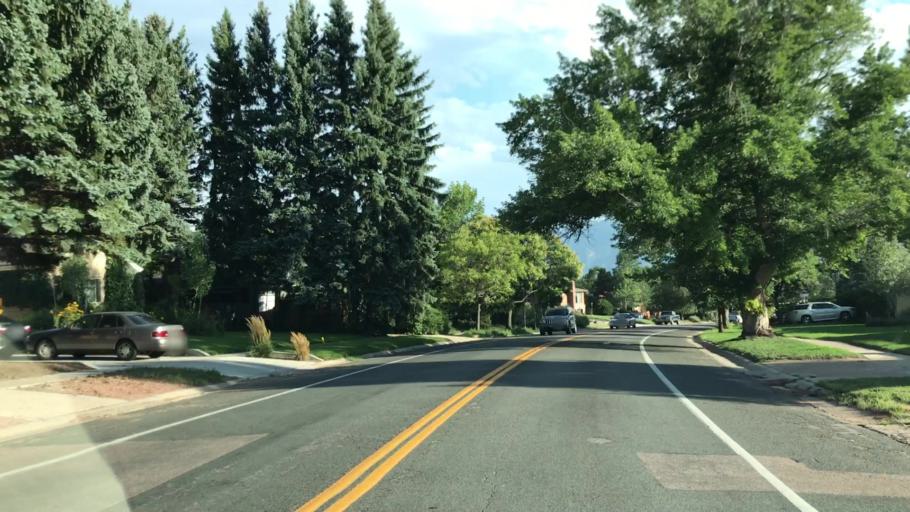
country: US
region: Colorado
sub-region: El Paso County
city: Colorado Springs
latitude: 38.8585
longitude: -104.8646
